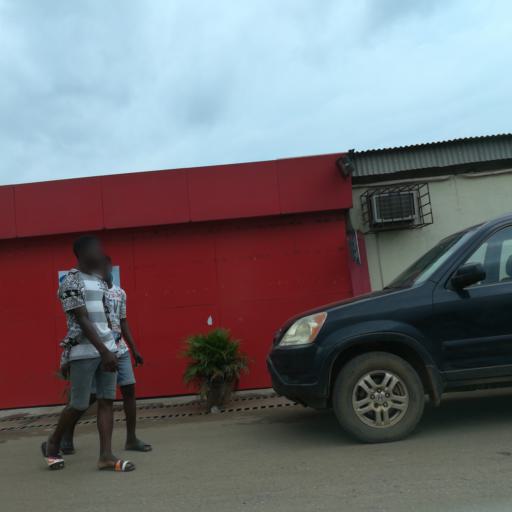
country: NG
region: Lagos
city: Agege
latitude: 6.6063
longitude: 3.2969
